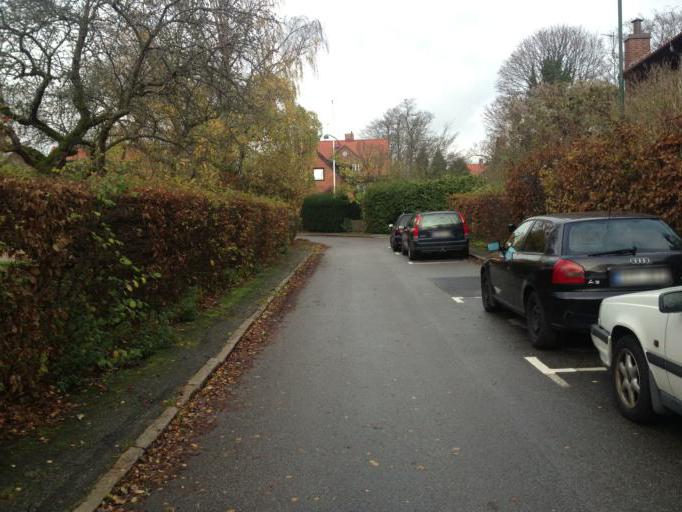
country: SE
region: Skane
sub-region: Lunds Kommun
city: Lund
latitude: 55.7060
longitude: 13.2084
